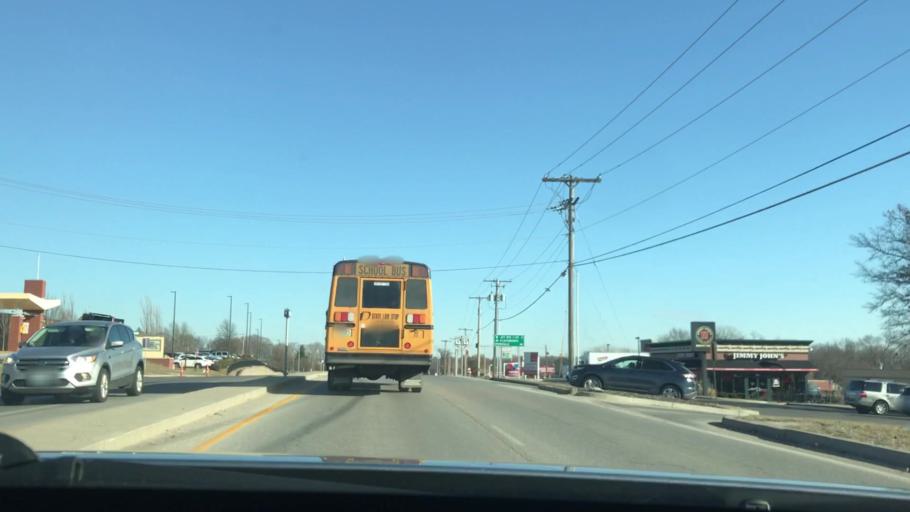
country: US
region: Missouri
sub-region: Platte County
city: Parkville
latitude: 39.2108
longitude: -94.6844
